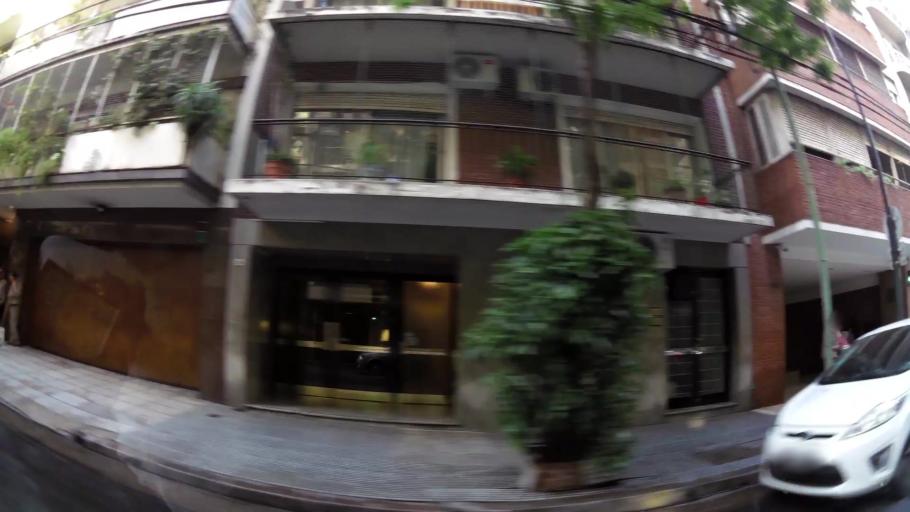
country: AR
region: Buenos Aires F.D.
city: Retiro
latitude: -34.5905
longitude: -58.3958
